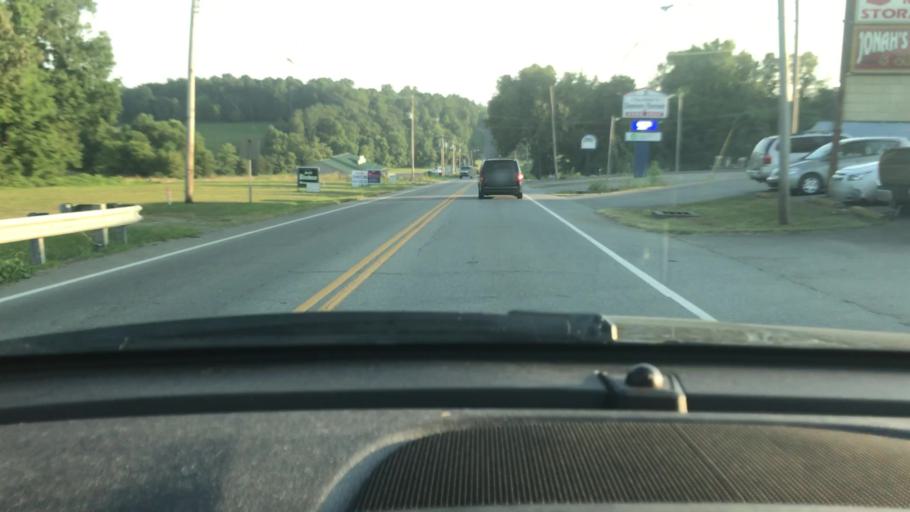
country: US
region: Tennessee
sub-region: Dickson County
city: Charlotte
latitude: 36.1672
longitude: -87.3511
